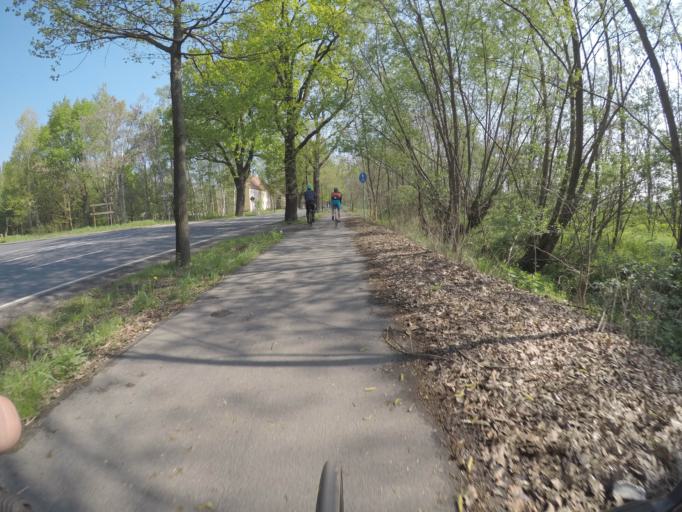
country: DE
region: Berlin
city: Buchholz
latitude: 52.6363
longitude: 13.4419
